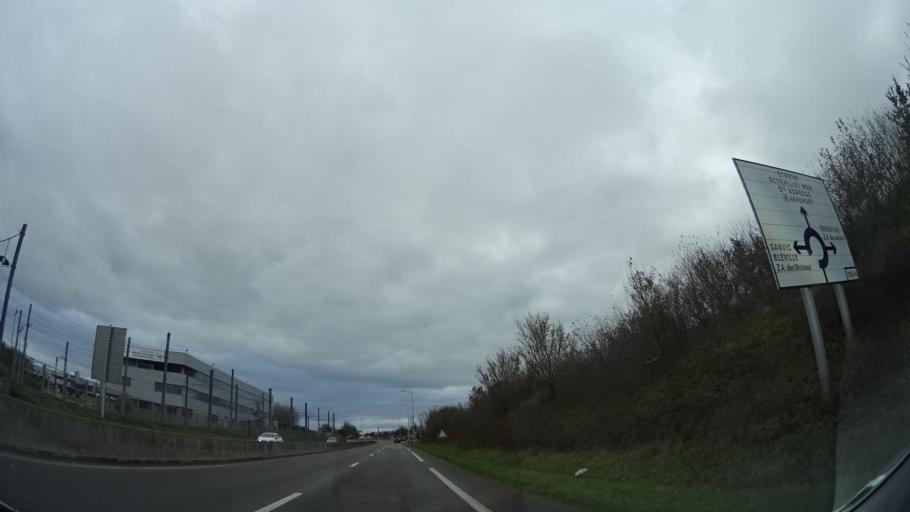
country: FR
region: Haute-Normandie
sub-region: Departement de la Seine-Maritime
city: Octeville-sur-Mer
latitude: 49.5316
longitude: 0.1060
